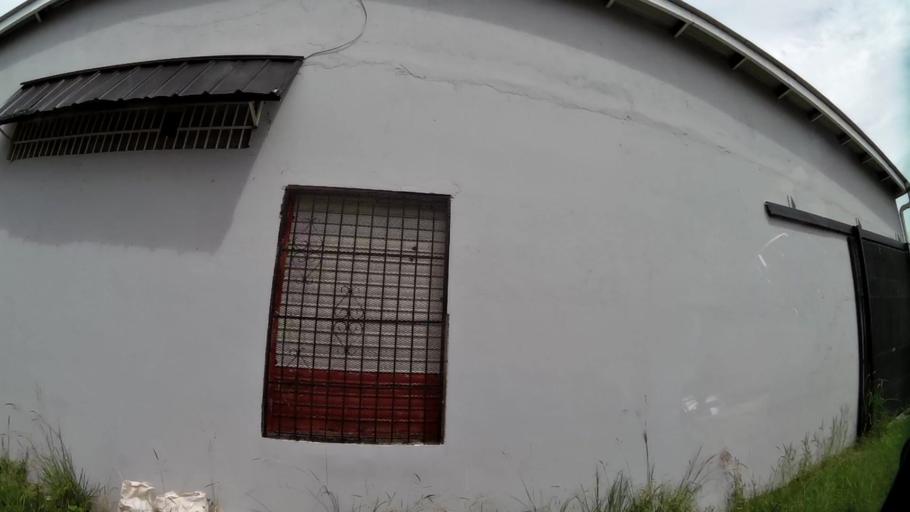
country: PA
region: Panama
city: San Miguelito
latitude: 9.0518
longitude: -79.4234
